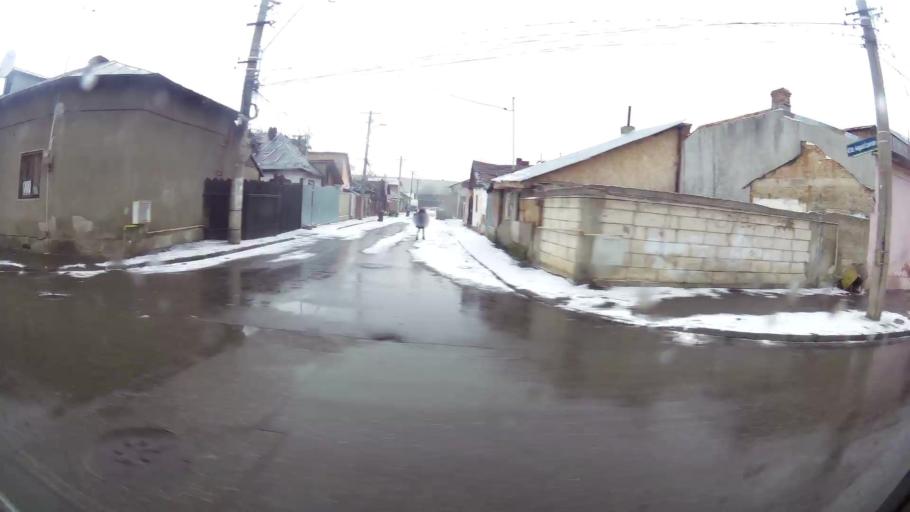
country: RO
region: Prahova
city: Ploiesti
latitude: 44.9509
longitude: 26.0257
